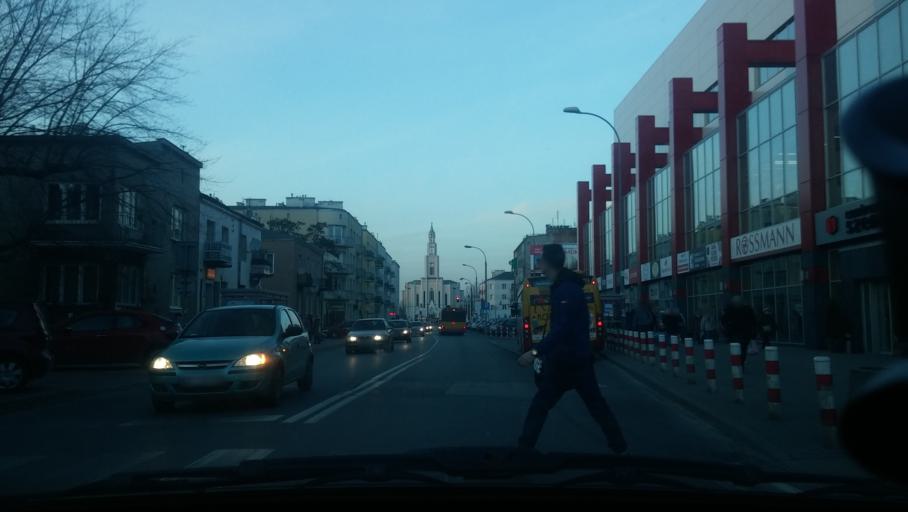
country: PL
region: Masovian Voivodeship
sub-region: Warszawa
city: Praga Poludnie
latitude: 52.2406
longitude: 21.1011
